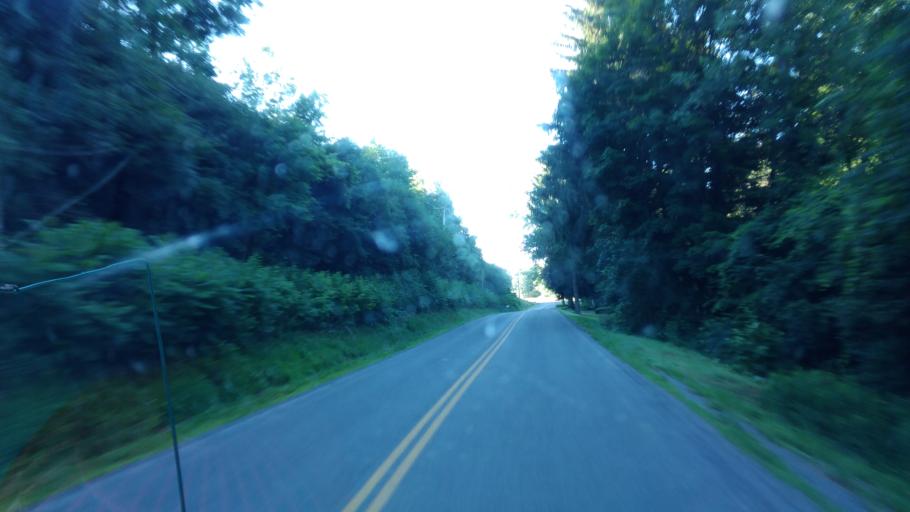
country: US
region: New York
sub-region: Wayne County
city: Lyons
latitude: 43.0809
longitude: -77.0167
